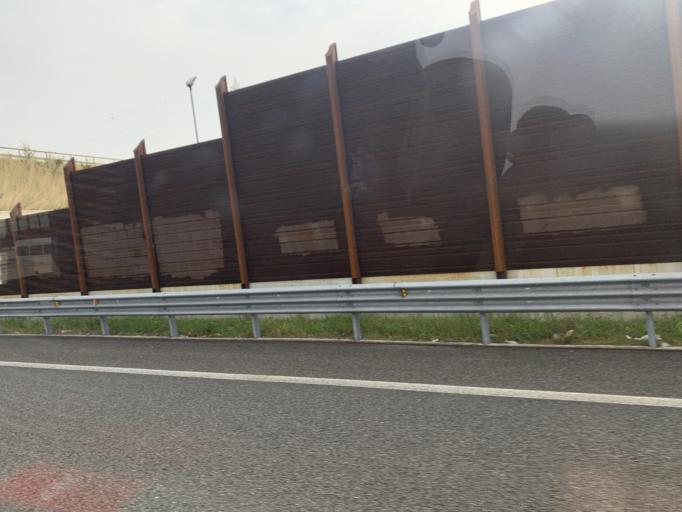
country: IT
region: Lombardy
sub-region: Provincia di Monza e Brianza
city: Caponago
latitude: 45.5724
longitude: 9.3800
